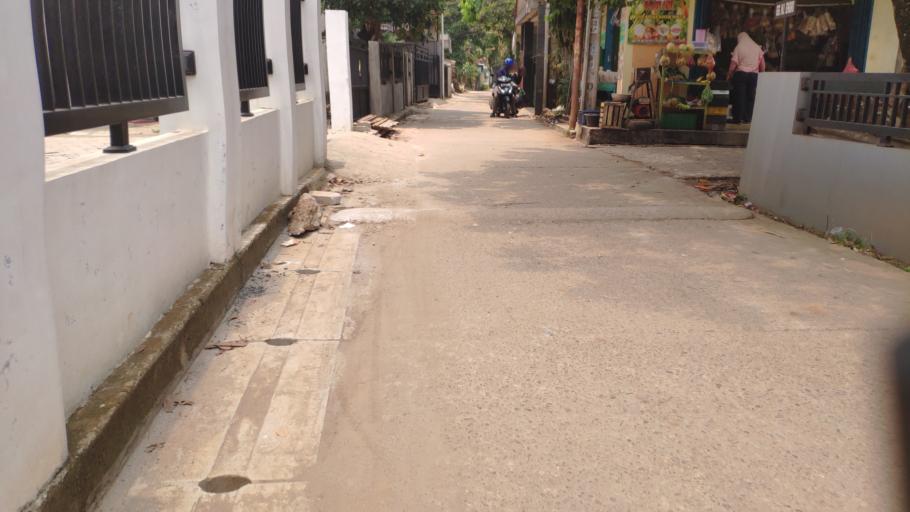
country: ID
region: West Java
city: Sawangan
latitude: -6.3818
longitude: 106.7886
